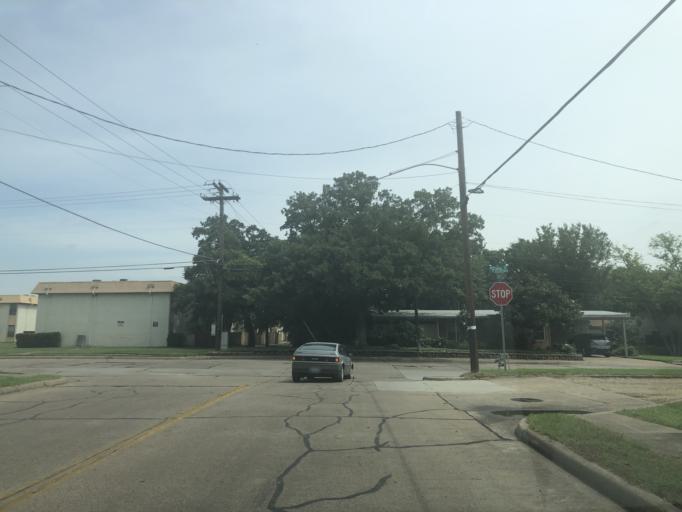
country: US
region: Texas
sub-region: Dallas County
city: Irving
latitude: 32.8093
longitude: -96.9708
